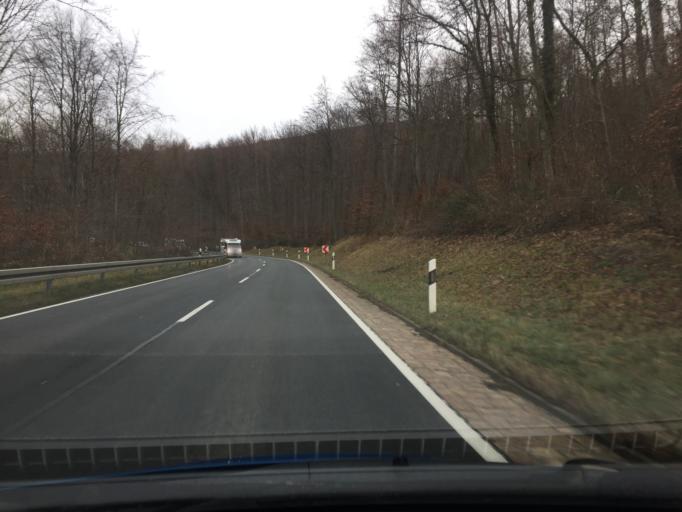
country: DE
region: Lower Saxony
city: Luerdissen
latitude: 51.9568
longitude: 9.6441
